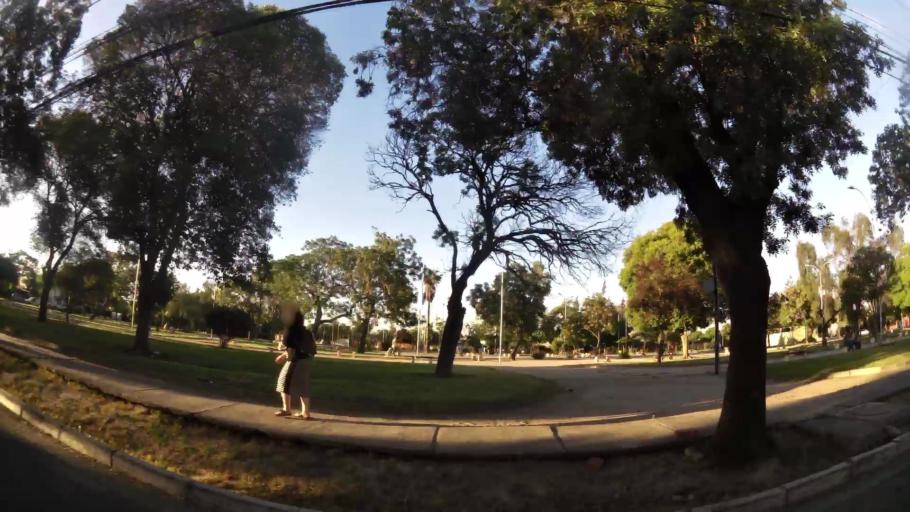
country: CL
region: Santiago Metropolitan
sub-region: Provincia de Maipo
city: San Bernardo
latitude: -33.5906
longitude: -70.6954
